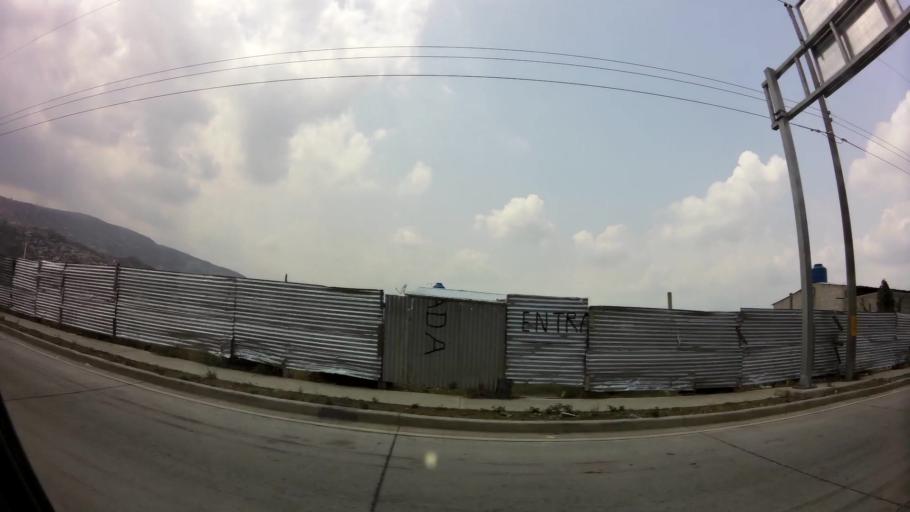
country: HN
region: Francisco Morazan
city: Tegucigalpa
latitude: 14.0839
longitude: -87.2420
